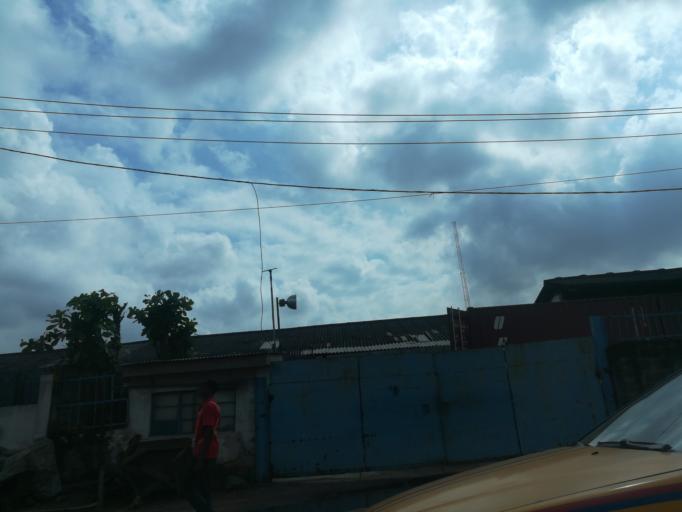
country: NG
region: Lagos
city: Somolu
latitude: 6.5483
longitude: 3.3570
